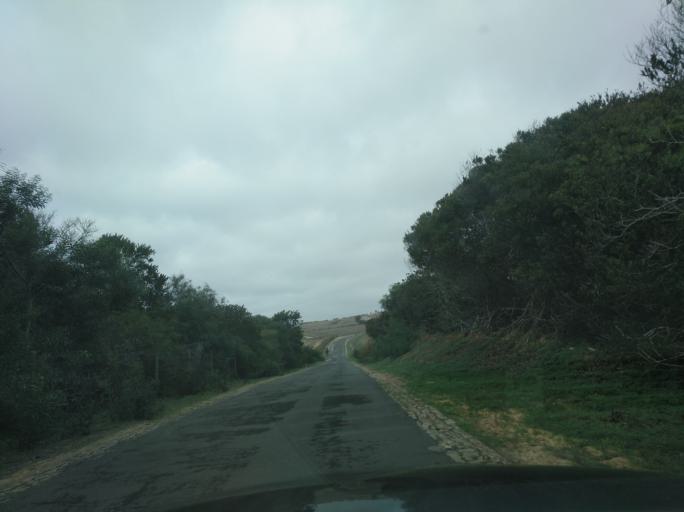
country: PT
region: Setubal
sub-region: Sines
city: Porto Covo
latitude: 37.8362
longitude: -8.7873
